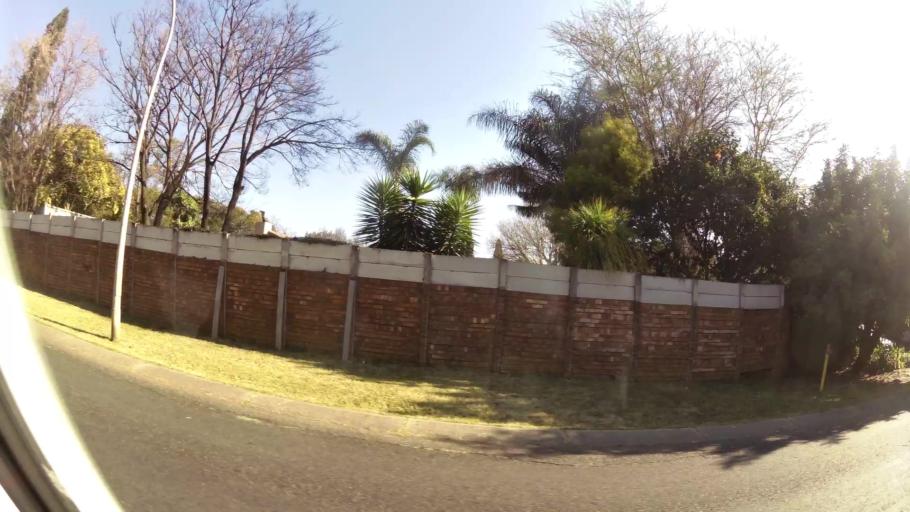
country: ZA
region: Gauteng
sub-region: City of Tshwane Metropolitan Municipality
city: Pretoria
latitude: -25.7996
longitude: 28.3012
